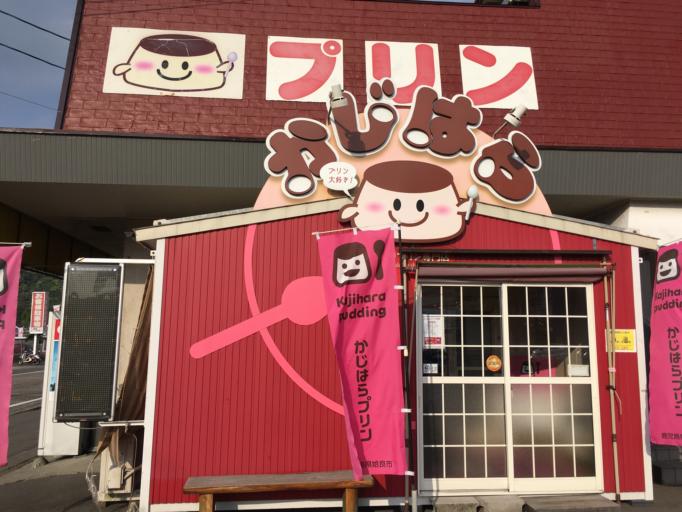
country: JP
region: Kagoshima
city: Kajiki
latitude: 31.7331
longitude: 130.6382
